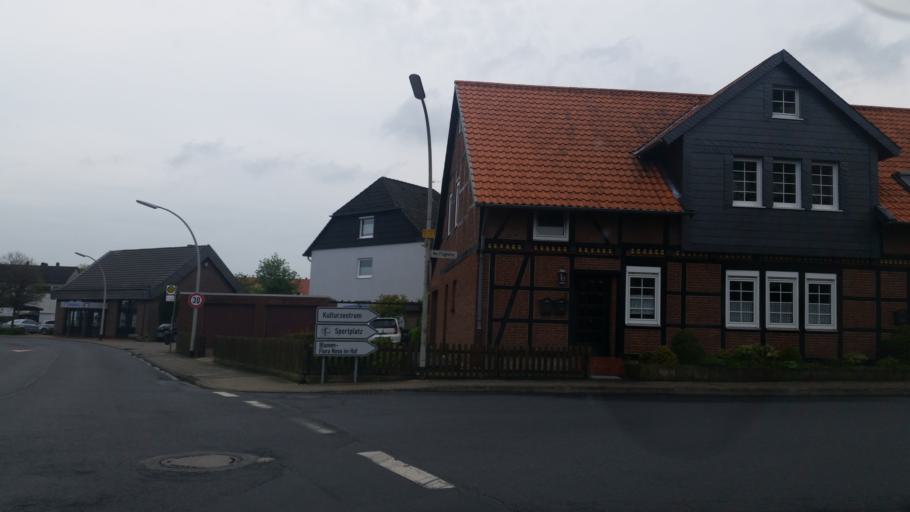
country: DE
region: Lower Saxony
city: Vordorf
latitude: 52.3255
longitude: 10.5585
